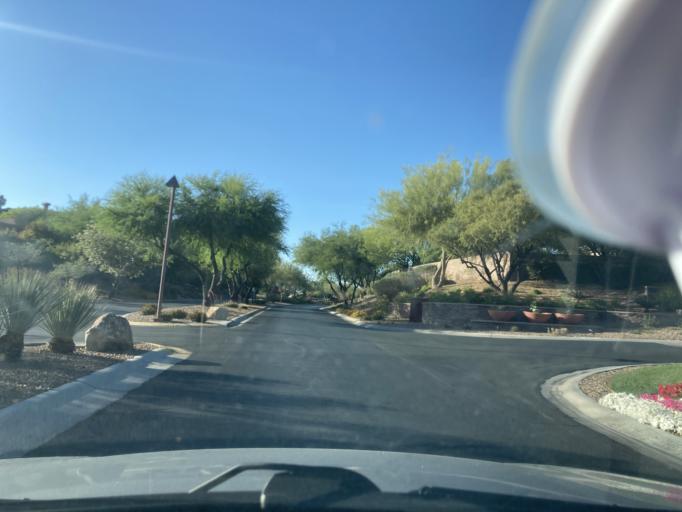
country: US
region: Nevada
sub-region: Clark County
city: Summerlin South
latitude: 36.1229
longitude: -115.3450
